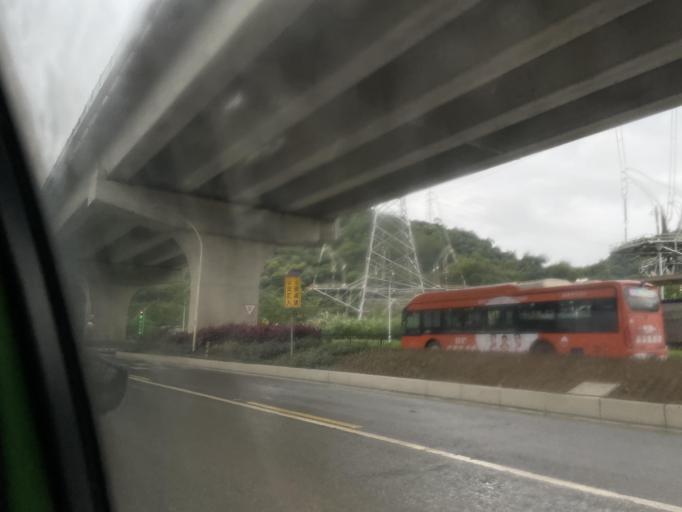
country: CN
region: Guangdong
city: Nanping
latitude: 22.1765
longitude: 113.4724
